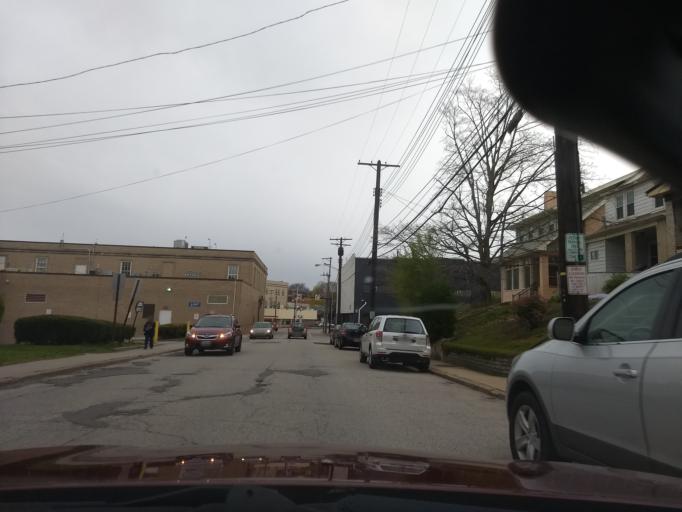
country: US
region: Pennsylvania
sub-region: Allegheny County
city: Dormont
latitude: 40.3955
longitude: -80.0316
